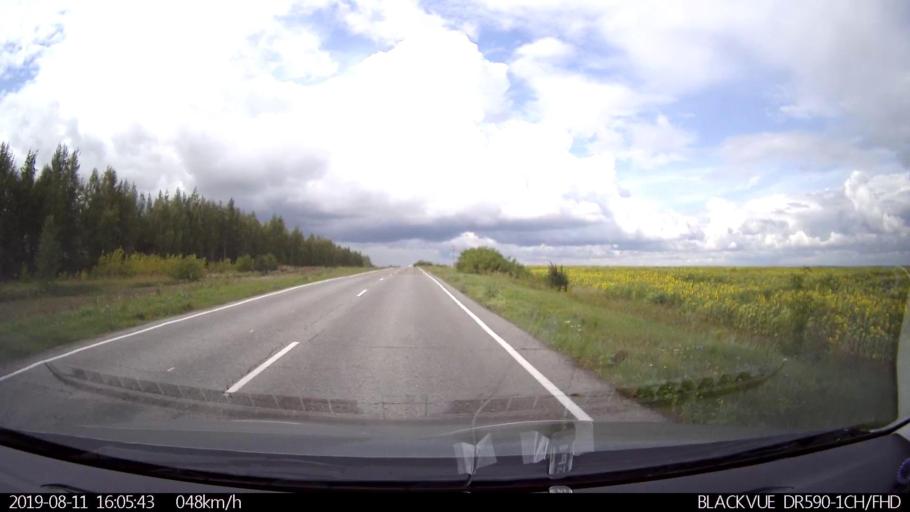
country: RU
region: Ulyanovsk
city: Ignatovka
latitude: 53.9628
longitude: 47.6491
